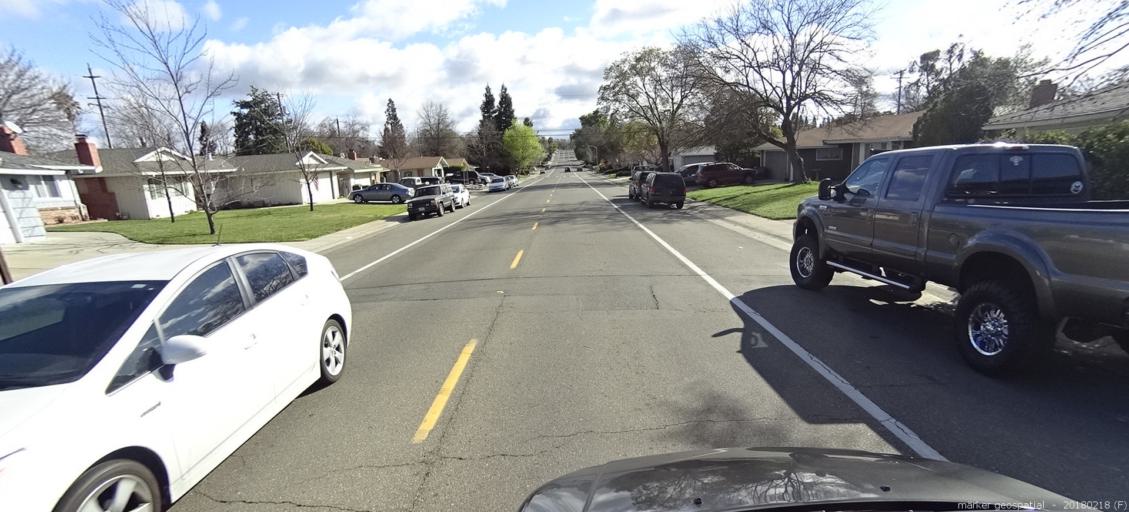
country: US
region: California
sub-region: Sacramento County
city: Orangevale
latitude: 38.6705
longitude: -121.2159
